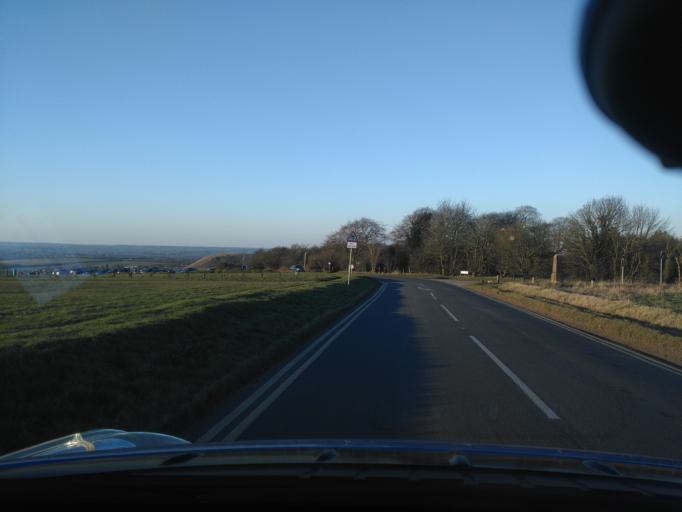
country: GB
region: England
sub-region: Central Bedfordshire
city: Dunstable
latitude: 51.8664
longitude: -0.5363
